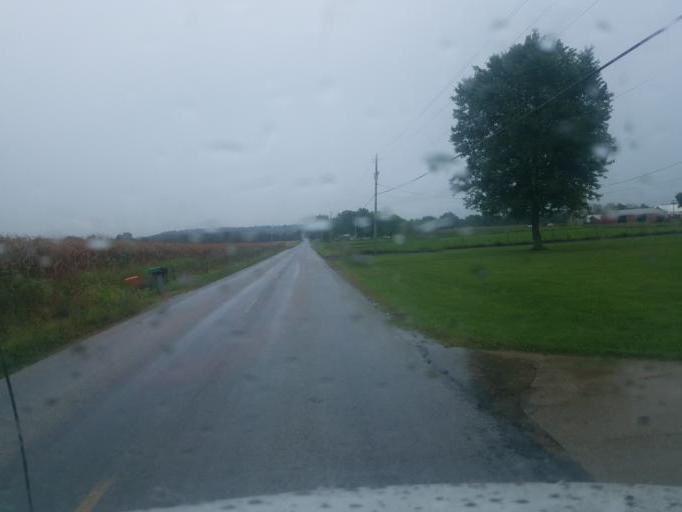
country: US
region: Ohio
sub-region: Wayne County
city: Creston
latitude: 40.9824
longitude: -81.8672
